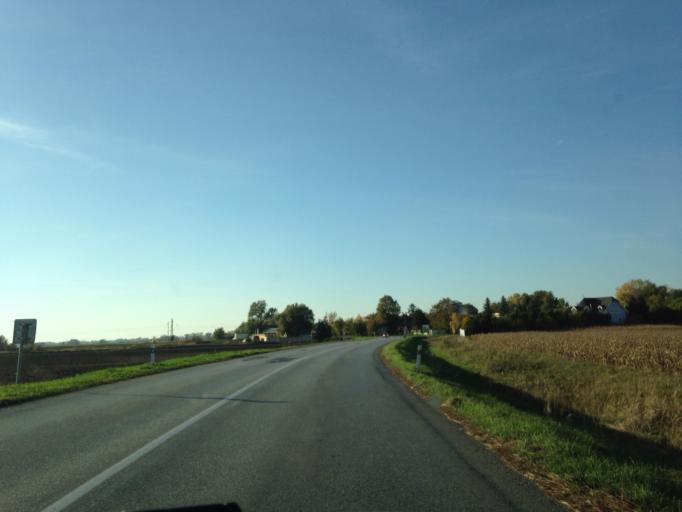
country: SK
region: Nitriansky
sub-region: Okres Komarno
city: Hurbanovo
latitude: 47.8057
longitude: 18.1938
